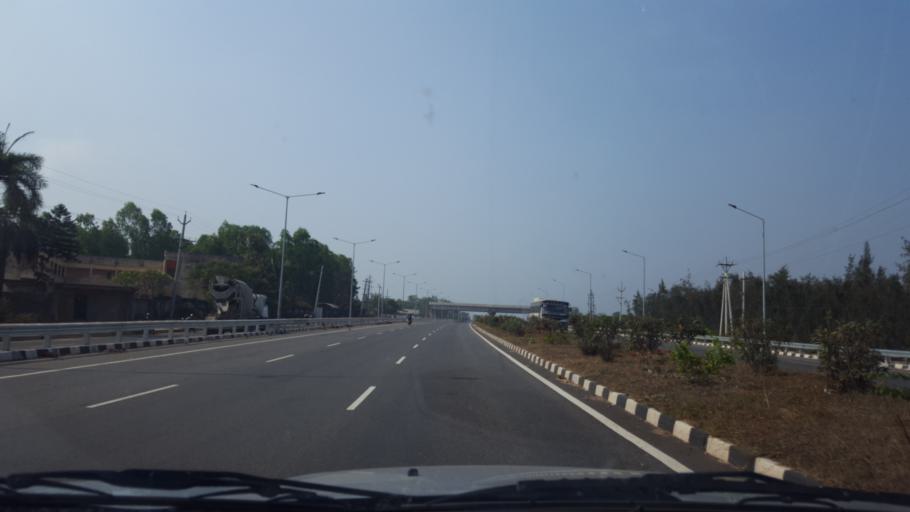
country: IN
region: Andhra Pradesh
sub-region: Vishakhapatnam
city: Bhimunipatnam
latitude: 17.9973
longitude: 83.4740
